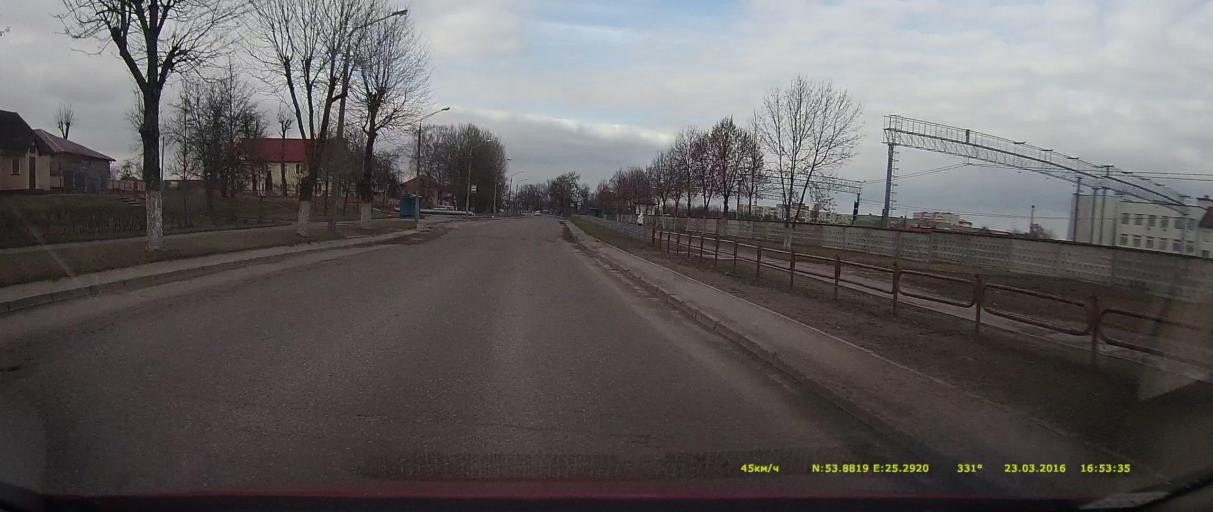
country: BY
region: Grodnenskaya
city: Lida
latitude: 53.8821
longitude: 25.2919
